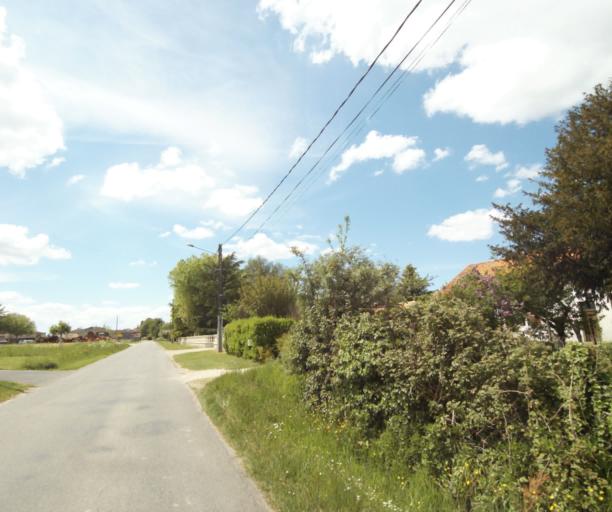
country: FR
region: Poitou-Charentes
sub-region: Departement de la Charente-Maritime
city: Burie
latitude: 45.7490
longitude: -0.4471
